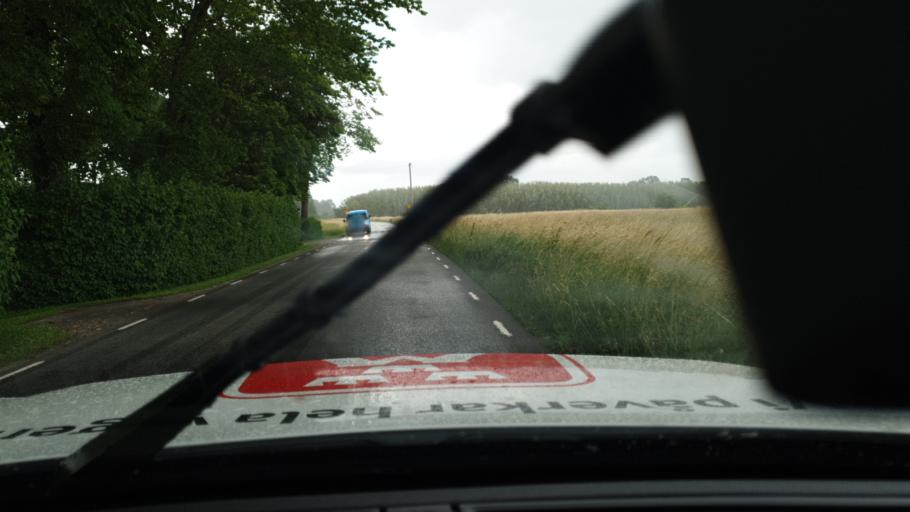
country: SE
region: Vaestra Goetaland
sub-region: Falkopings Kommun
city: Akarp
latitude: 58.2241
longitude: 13.6058
